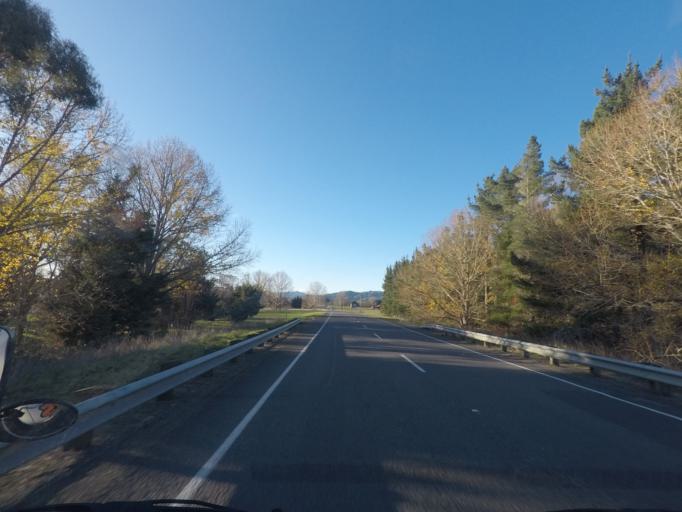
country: NZ
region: Canterbury
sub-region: Kaikoura District
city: Kaikoura
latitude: -42.7194
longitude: 173.2860
